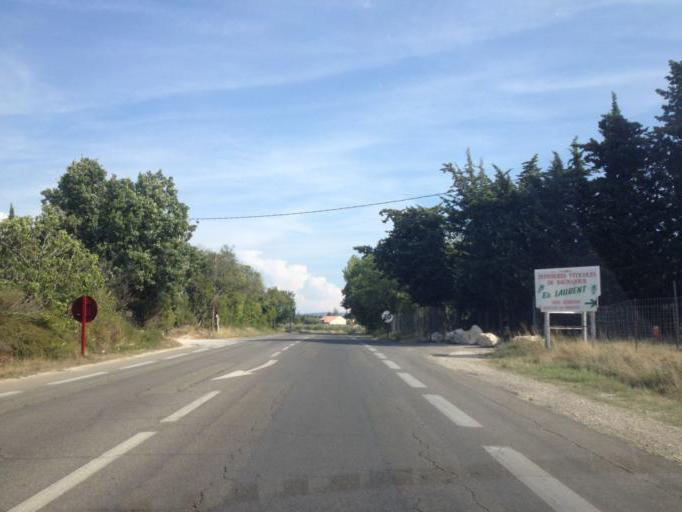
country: FR
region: Provence-Alpes-Cote d'Azur
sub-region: Departement du Vaucluse
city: Aubignan
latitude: 44.0810
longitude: 5.0383
